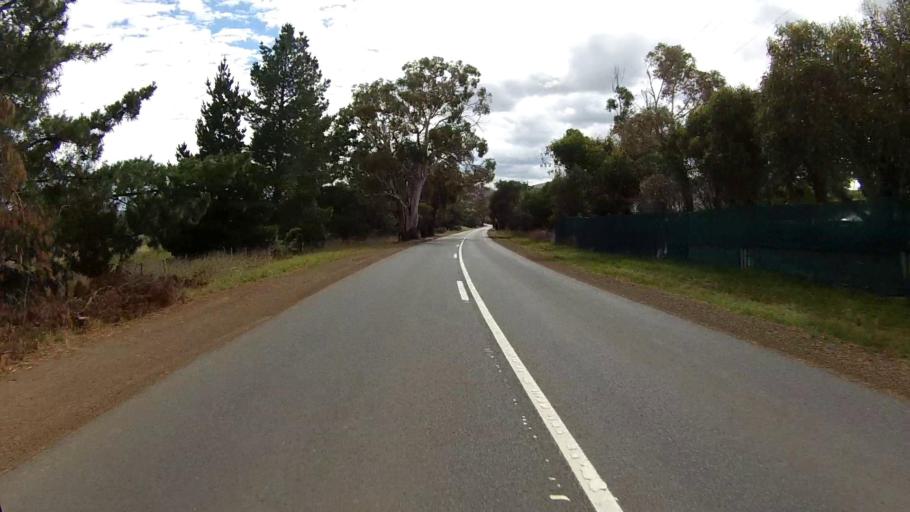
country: AU
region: Tasmania
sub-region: Clarence
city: Cambridge
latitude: -42.7627
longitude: 147.3956
